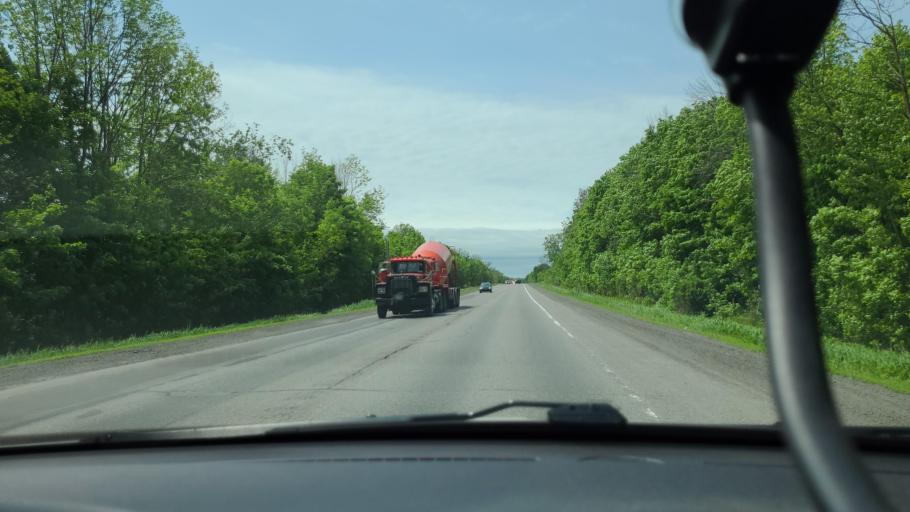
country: CA
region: Quebec
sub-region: Lanaudiere
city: Saint-Jacques
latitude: 45.9620
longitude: -73.5644
